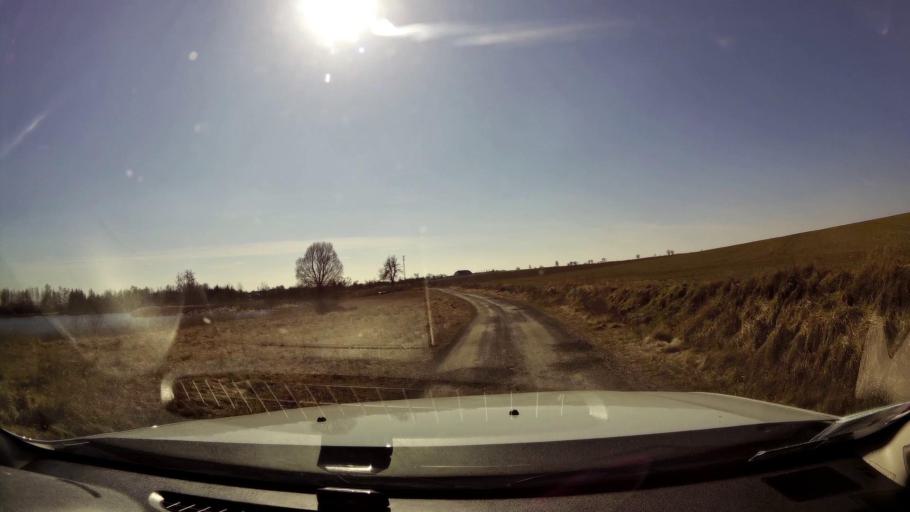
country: PL
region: West Pomeranian Voivodeship
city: Trzcinsko Zdroj
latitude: 52.9943
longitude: 14.6023
